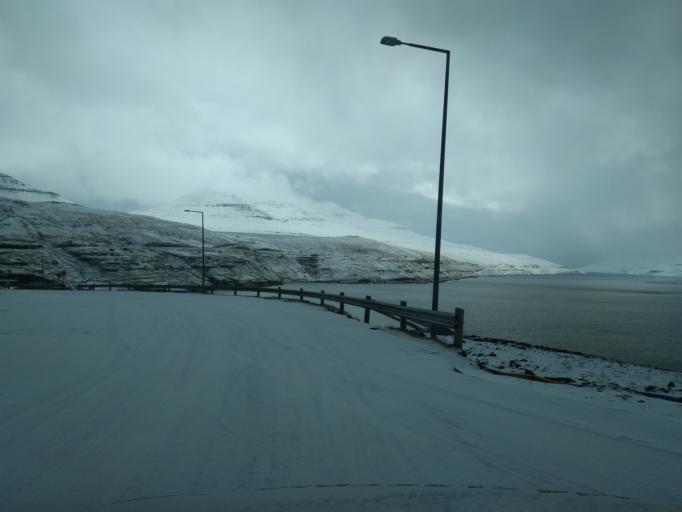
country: FO
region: Eysturoy
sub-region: Eidi
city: Eidi
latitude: 62.2996
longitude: -7.1000
